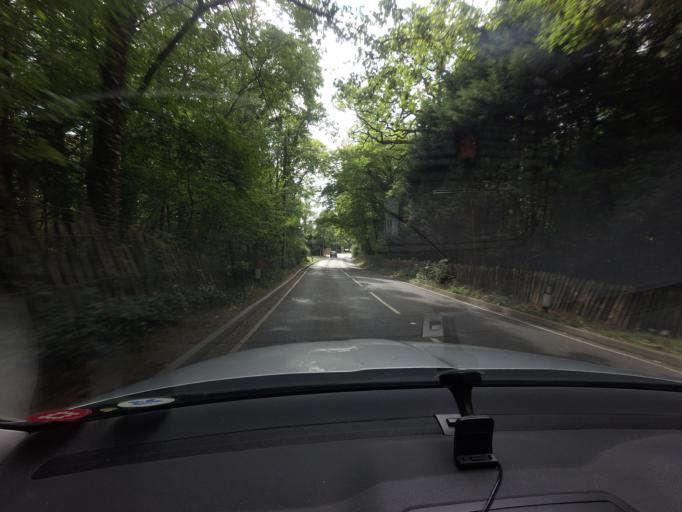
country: GB
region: England
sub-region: Kent
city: Tonbridge
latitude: 51.2217
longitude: 0.2881
